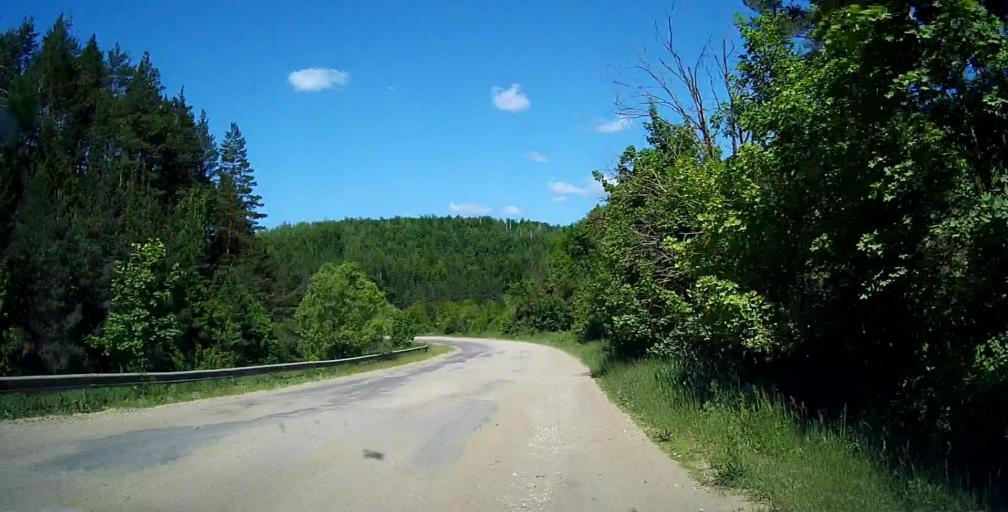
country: RU
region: Tula
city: Kurkino
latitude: 53.1997
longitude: 38.5698
